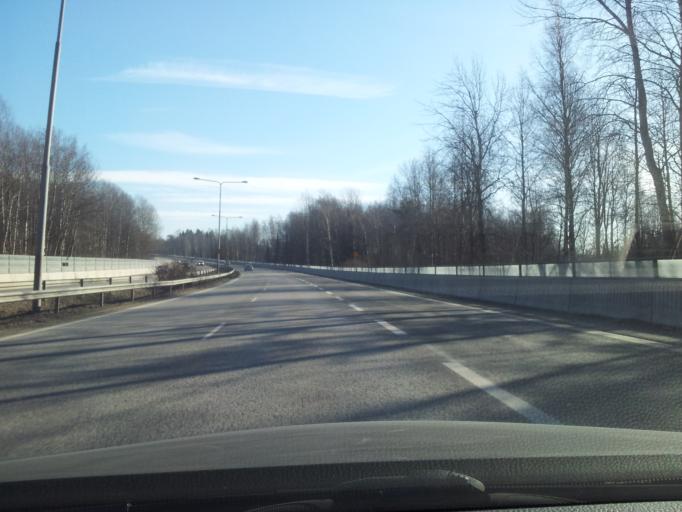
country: FI
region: Uusimaa
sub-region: Helsinki
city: Teekkarikylae
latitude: 60.2025
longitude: 24.8612
